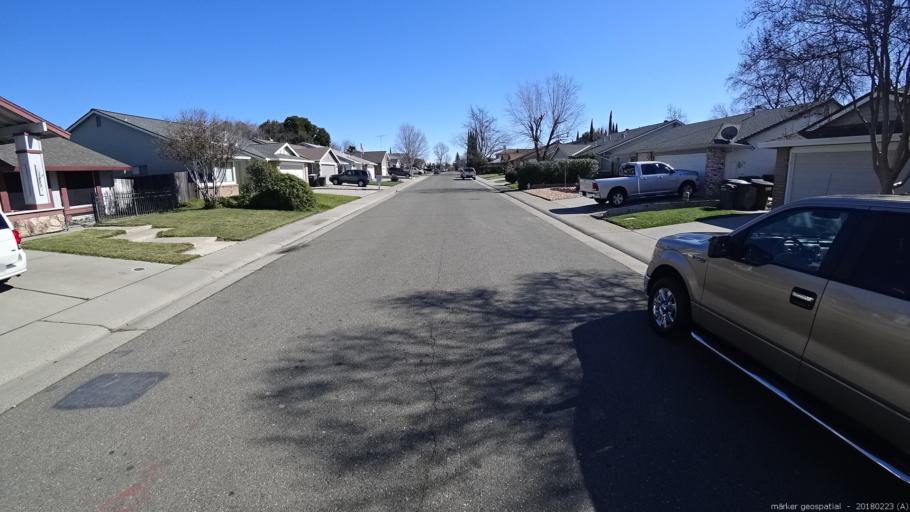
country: US
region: California
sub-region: Sacramento County
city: North Highlands
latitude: 38.7051
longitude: -121.3727
